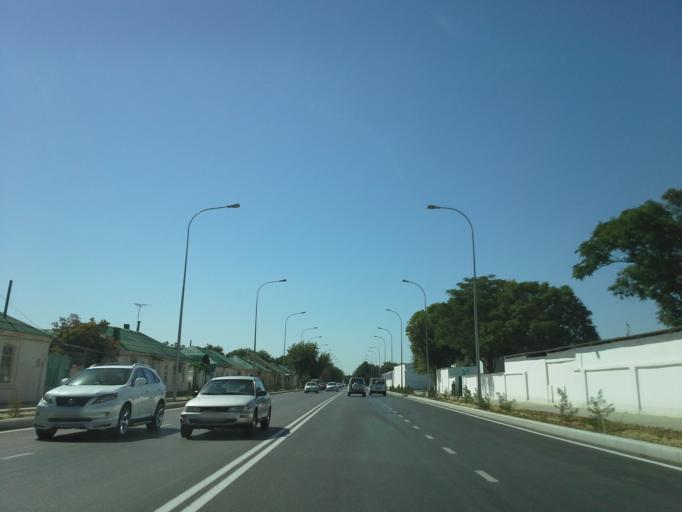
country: TM
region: Ahal
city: Ashgabat
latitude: 37.9537
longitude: 58.3852
